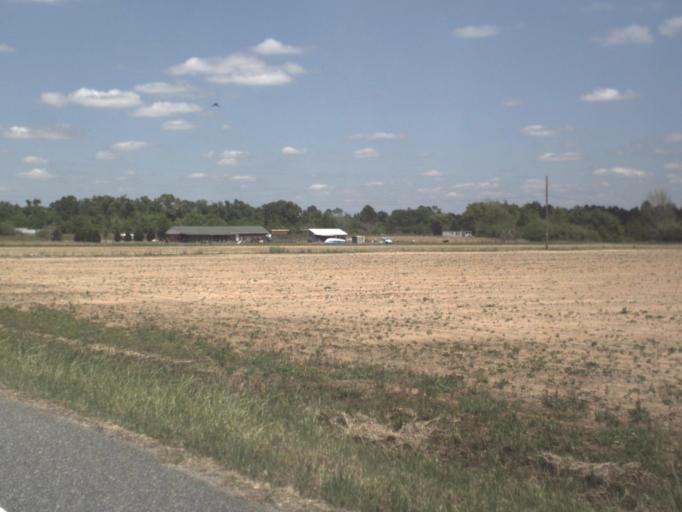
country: US
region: Florida
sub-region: Santa Rosa County
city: Point Baker
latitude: 30.8556
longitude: -87.0528
